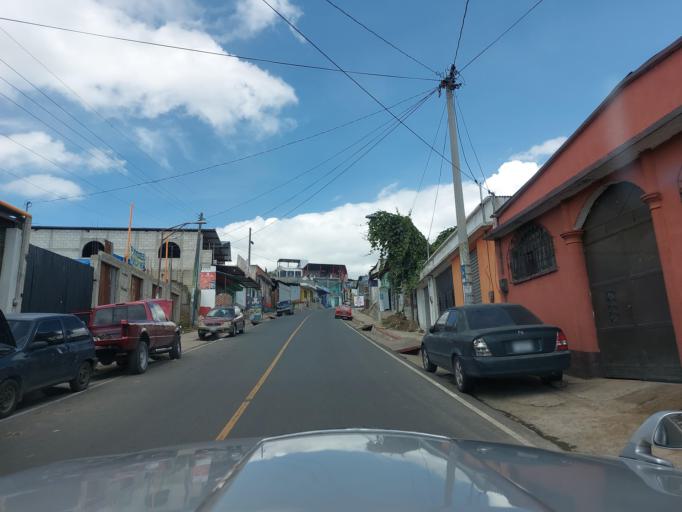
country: GT
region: Chimaltenango
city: San Andres Itzapa
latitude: 14.6222
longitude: -90.8372
